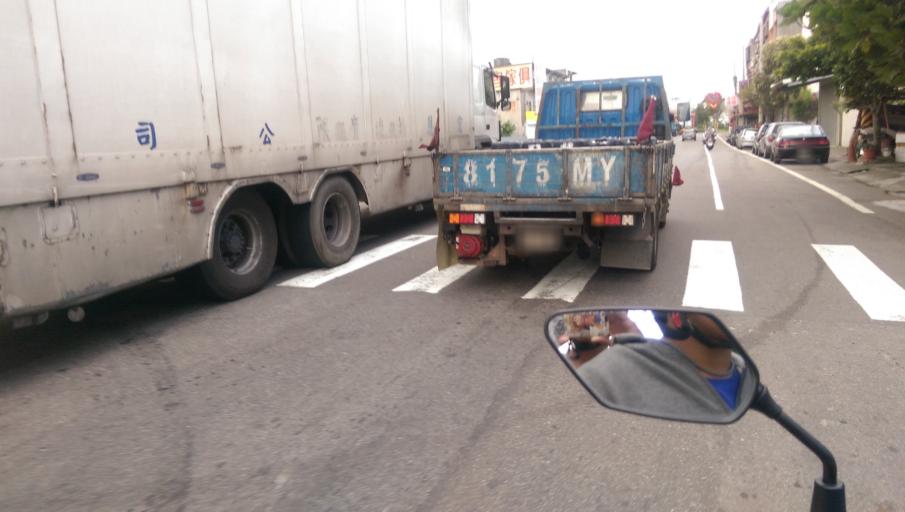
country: TW
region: Taiwan
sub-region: Hsinchu
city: Hsinchu
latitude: 24.8256
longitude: 120.9274
